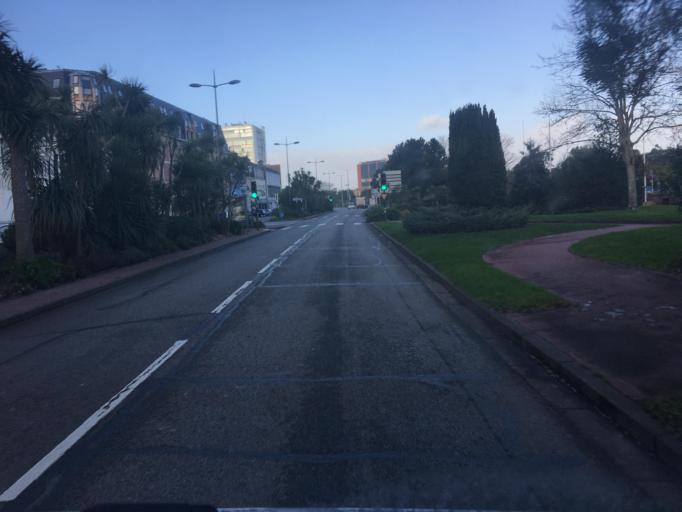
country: FR
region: Lower Normandy
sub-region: Departement de la Manche
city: Cherbourg-Octeville
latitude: 49.6435
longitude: -1.6253
